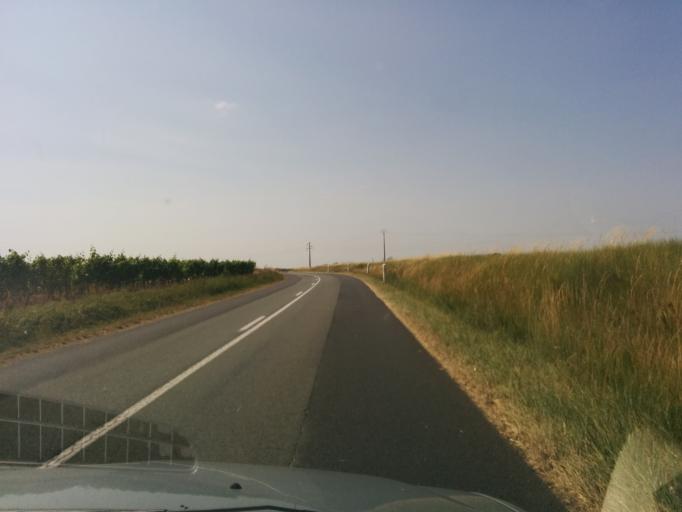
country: FR
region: Poitou-Charentes
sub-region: Departement de la Vienne
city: Mirebeau
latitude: 46.7712
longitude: 0.1452
